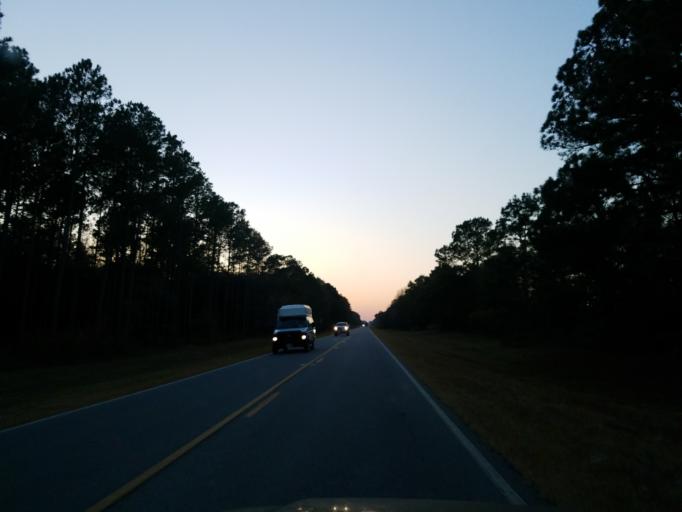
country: US
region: Georgia
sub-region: Turner County
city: Ashburn
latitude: 31.7212
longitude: -83.4689
